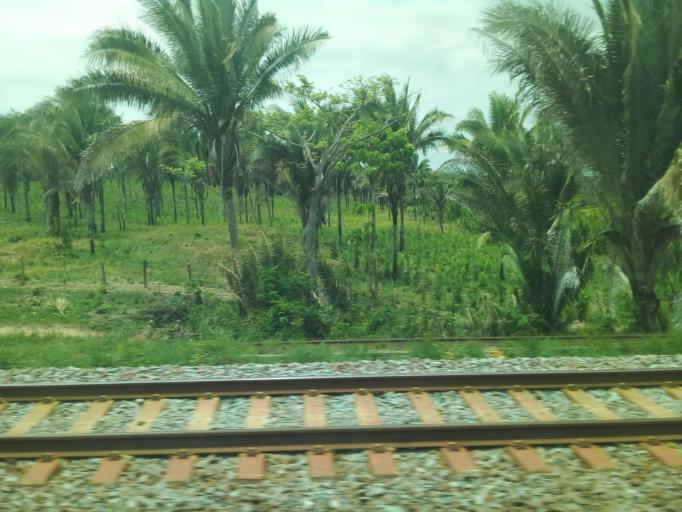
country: BR
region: Maranhao
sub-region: Santa Ines
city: Santa Ines
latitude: -3.7163
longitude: -45.5427
